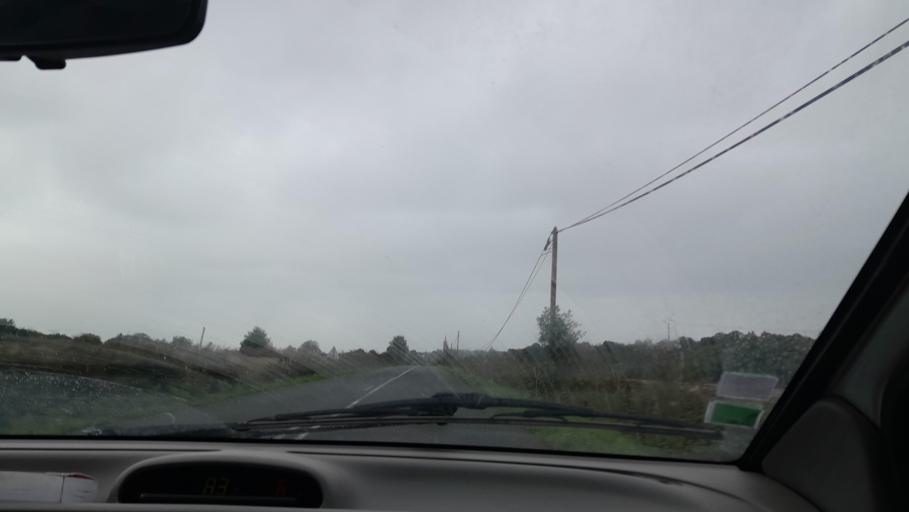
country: FR
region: Pays de la Loire
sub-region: Departement de Maine-et-Loire
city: Pouance
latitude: 47.7307
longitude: -1.1776
